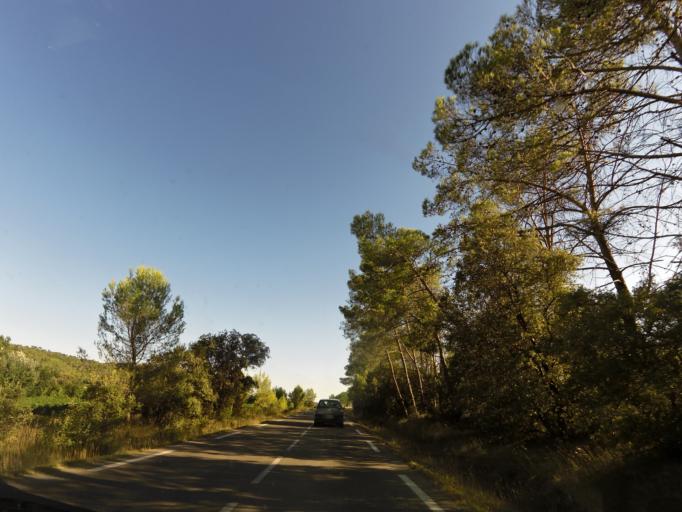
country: FR
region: Languedoc-Roussillon
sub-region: Departement du Gard
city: Quissac
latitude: 43.8601
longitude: 4.0170
